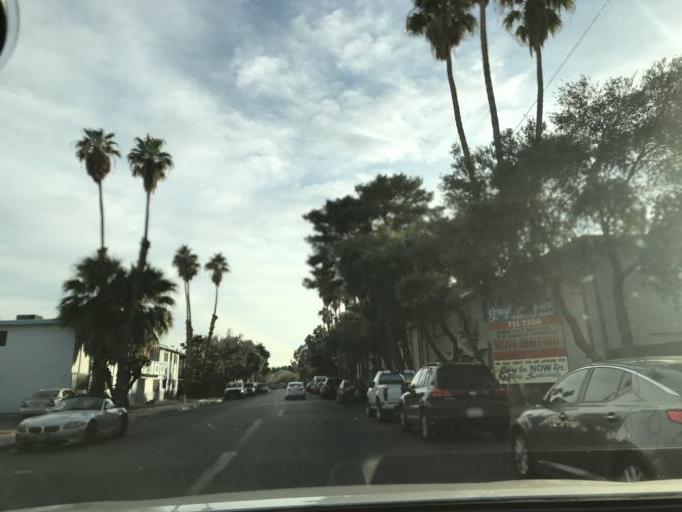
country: US
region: Nevada
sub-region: Clark County
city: Winchester
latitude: 36.1425
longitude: -115.1497
